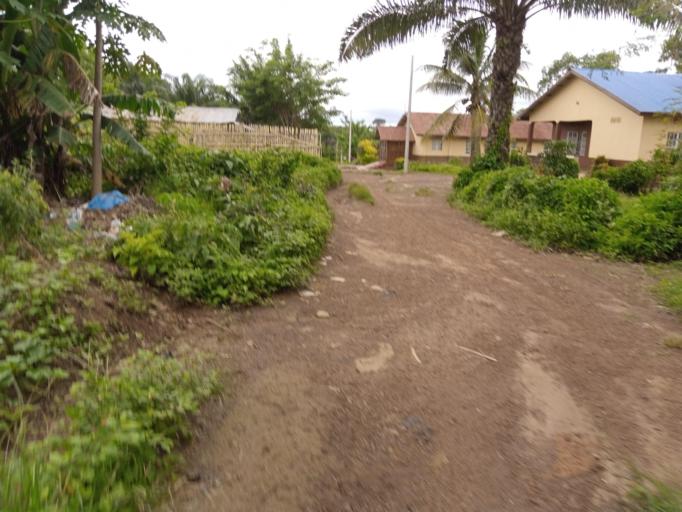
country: SL
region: Southern Province
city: Moyamba
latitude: 8.1676
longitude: -12.4270
